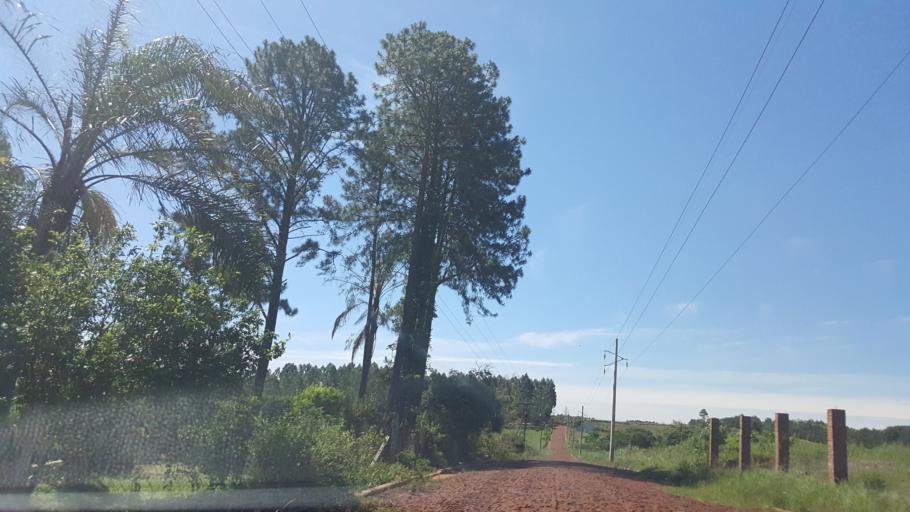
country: AR
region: Misiones
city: Capiovi
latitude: -26.9317
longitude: -55.0719
